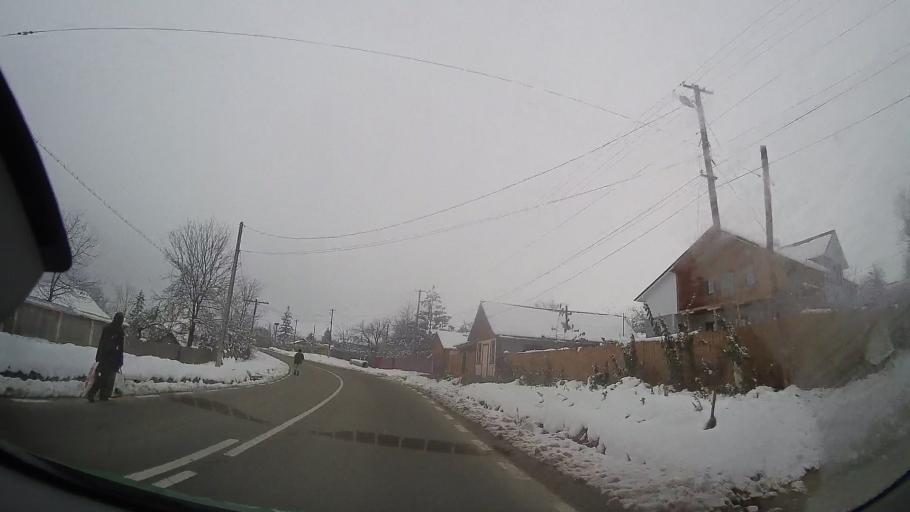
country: RO
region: Vaslui
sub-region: Comuna Todiresti
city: Todiresti
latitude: 46.8417
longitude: 27.3714
